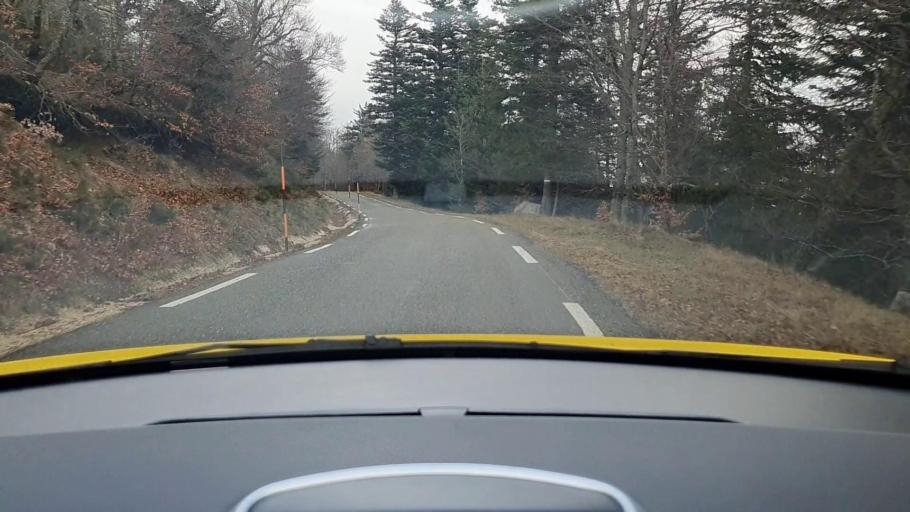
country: FR
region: Languedoc-Roussillon
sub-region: Departement du Gard
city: Branoux-les-Taillades
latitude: 44.3736
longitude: 3.9125
